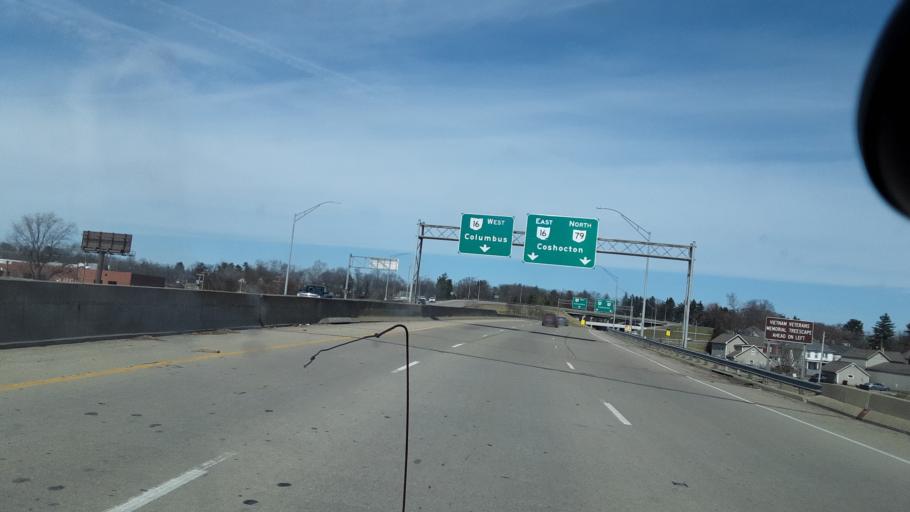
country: US
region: Ohio
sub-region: Licking County
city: Newark
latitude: 40.0565
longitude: -82.4200
